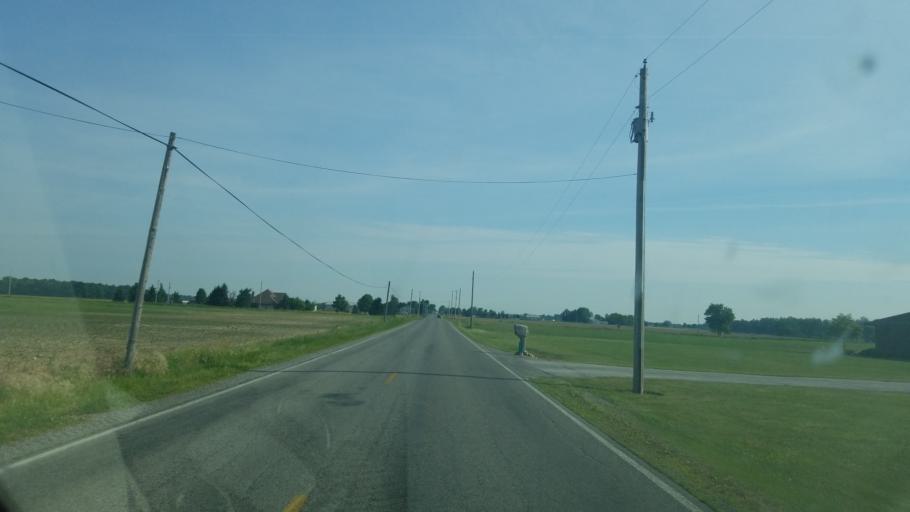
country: US
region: Ohio
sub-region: Hancock County
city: Findlay
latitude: 40.9775
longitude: -83.6985
